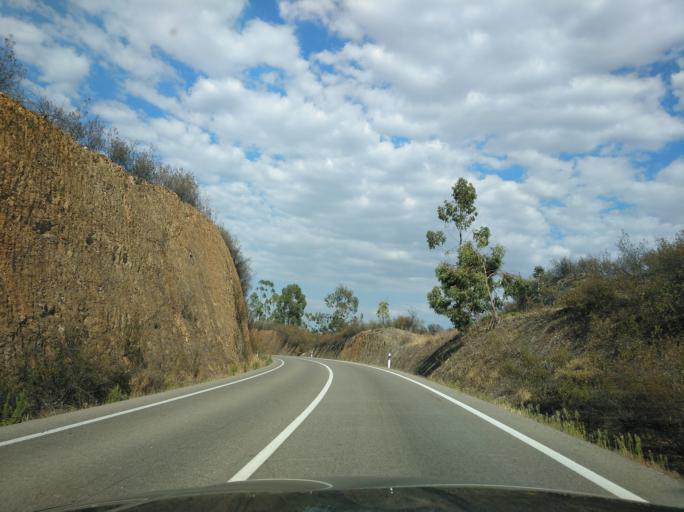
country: ES
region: Andalusia
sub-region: Provincia de Huelva
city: Rosal de la Frontera
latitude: 37.8829
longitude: -7.2050
